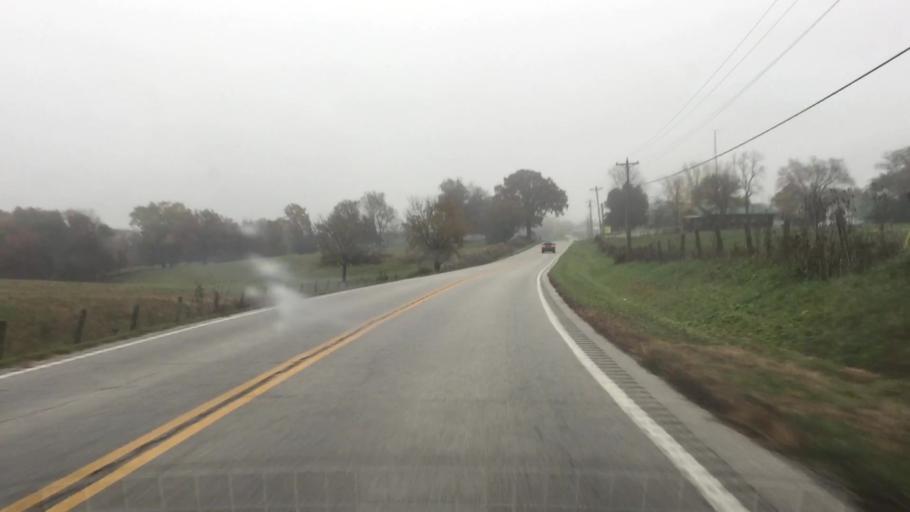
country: US
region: Missouri
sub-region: Callaway County
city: Fulton
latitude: 38.8628
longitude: -92.0059
